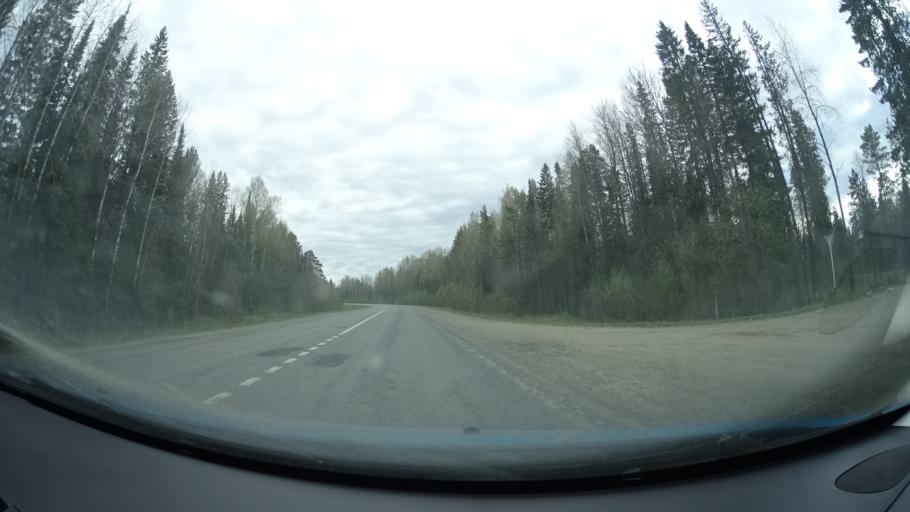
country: RU
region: Perm
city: Yugo-Kamskiy
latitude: 57.6498
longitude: 55.5980
